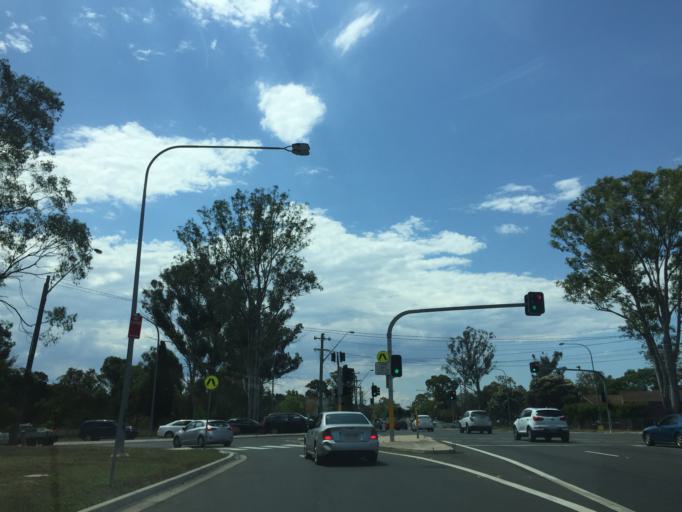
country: AU
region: New South Wales
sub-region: Blacktown
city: Doonside
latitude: -33.7558
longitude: 150.8645
